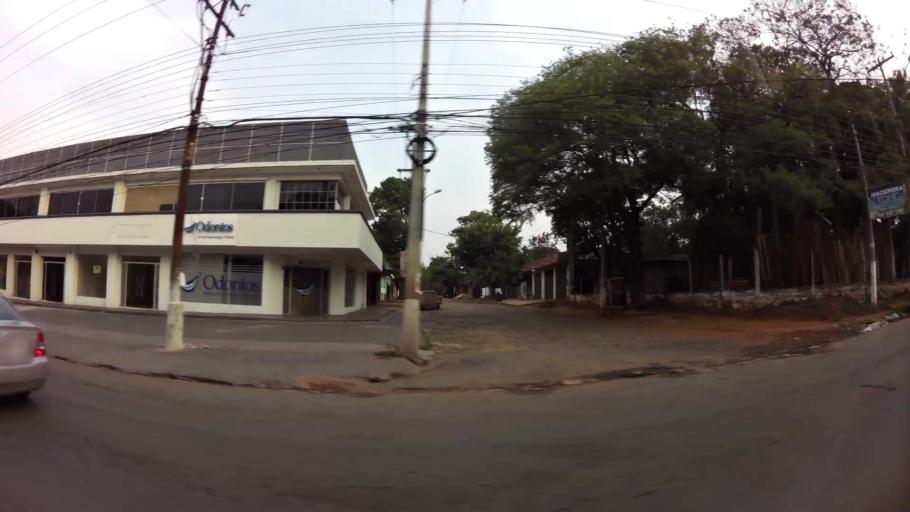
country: PY
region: Central
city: Lambare
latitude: -25.3397
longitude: -57.5928
